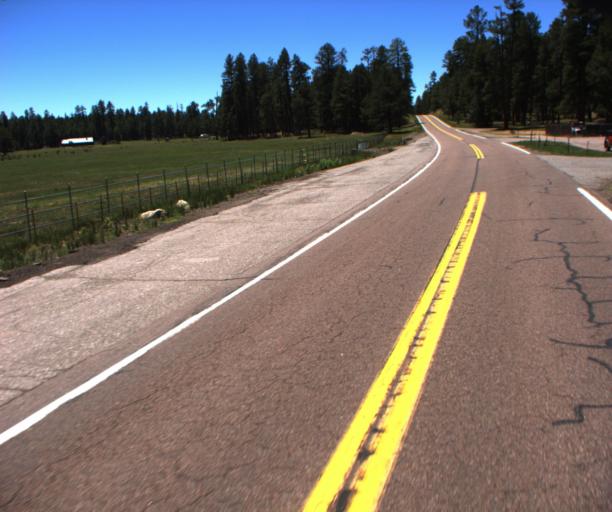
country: US
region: Arizona
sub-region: Gila County
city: Pine
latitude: 34.5459
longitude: -111.3220
